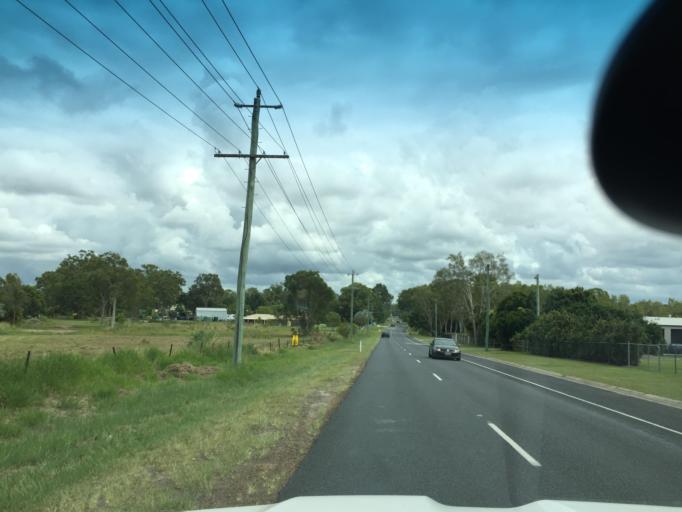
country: AU
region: Queensland
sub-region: Moreton Bay
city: Burpengary
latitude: -27.1281
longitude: 152.9859
